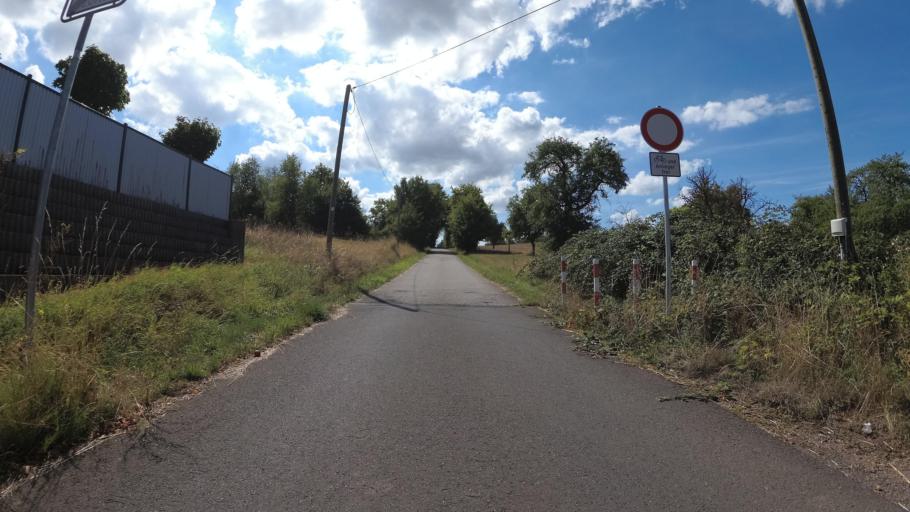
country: DE
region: Saarland
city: Mainzweiler
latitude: 49.4189
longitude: 7.1114
